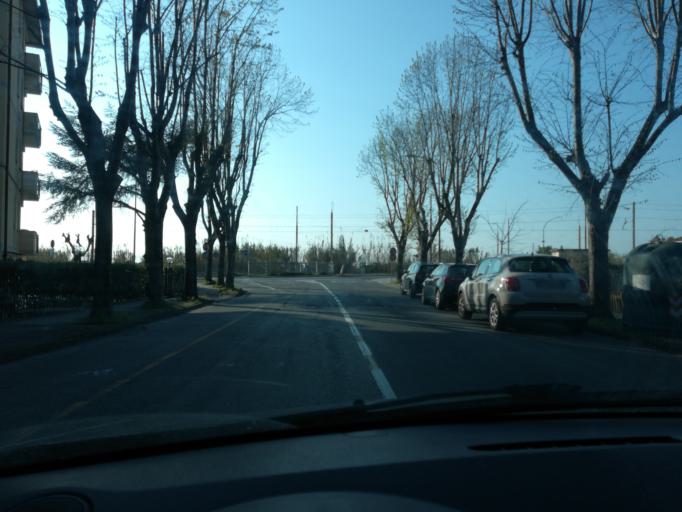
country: IT
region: Tuscany
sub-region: Province of Pisa
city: Pisa
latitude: 43.7336
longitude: 10.4012
